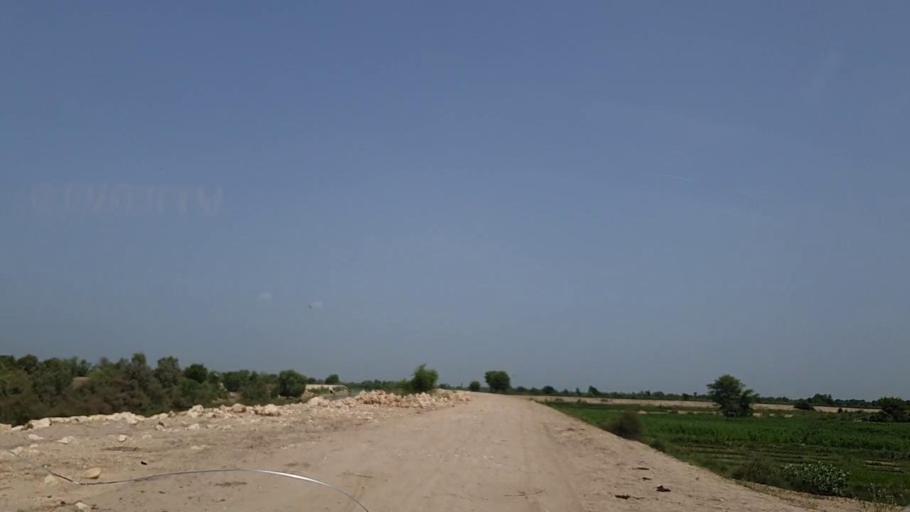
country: PK
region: Sindh
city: Kandiaro
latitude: 27.0571
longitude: 68.1329
